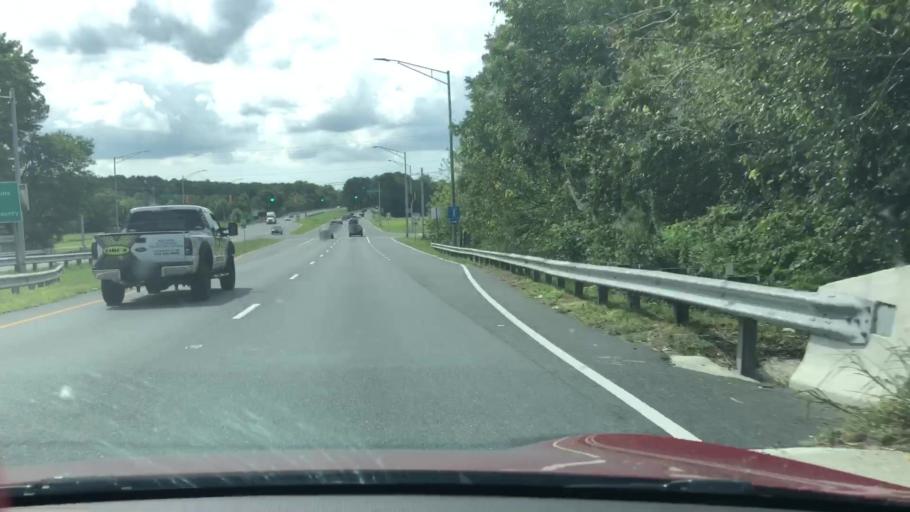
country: US
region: Maryland
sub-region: Worcester County
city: Pocomoke City
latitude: 38.0790
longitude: -75.5752
